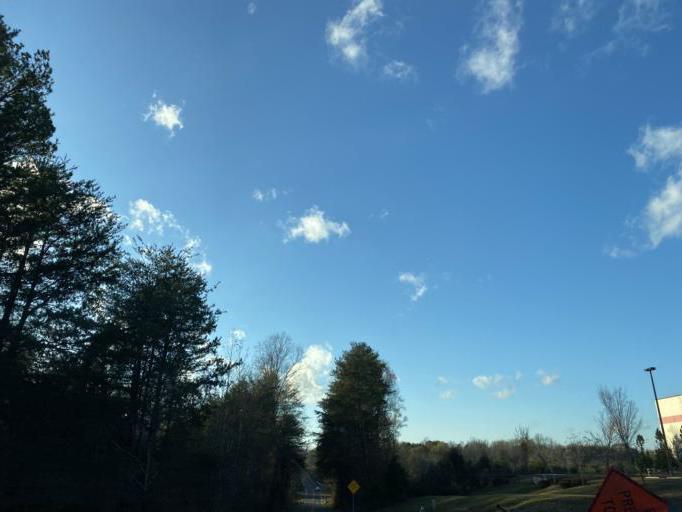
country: US
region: South Carolina
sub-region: York County
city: Clover
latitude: 35.1277
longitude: -81.2230
